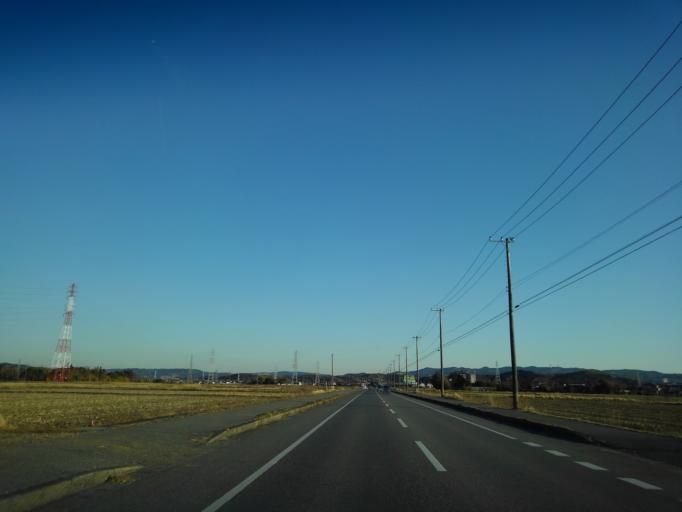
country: JP
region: Chiba
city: Kimitsu
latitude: 35.3173
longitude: 139.9088
